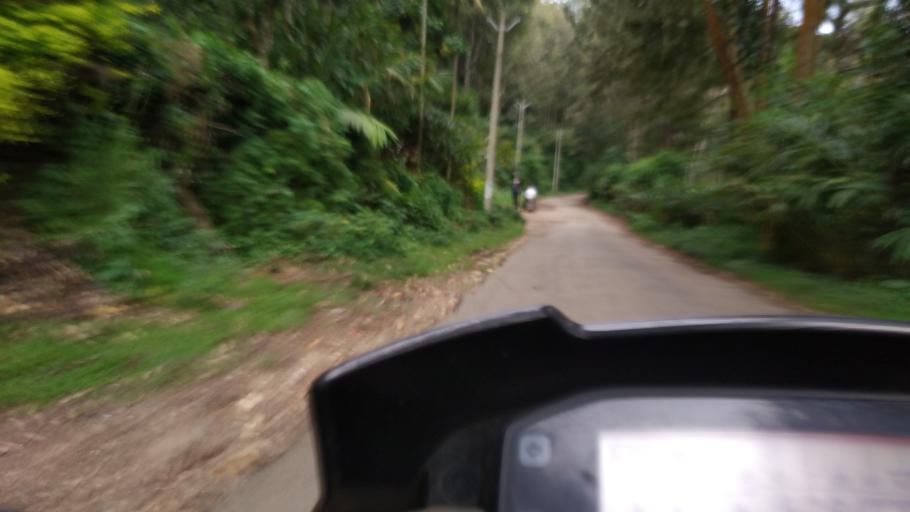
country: IN
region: Tamil Nadu
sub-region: Theni
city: Bodinayakkanur
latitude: 10.0282
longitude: 77.2312
